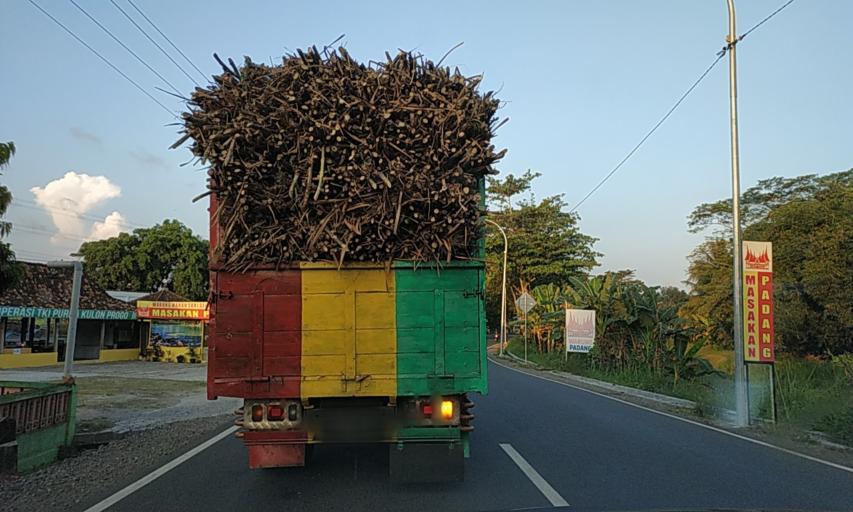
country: ID
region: Daerah Istimewa Yogyakarta
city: Srandakan
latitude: -7.8835
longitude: 110.0464
